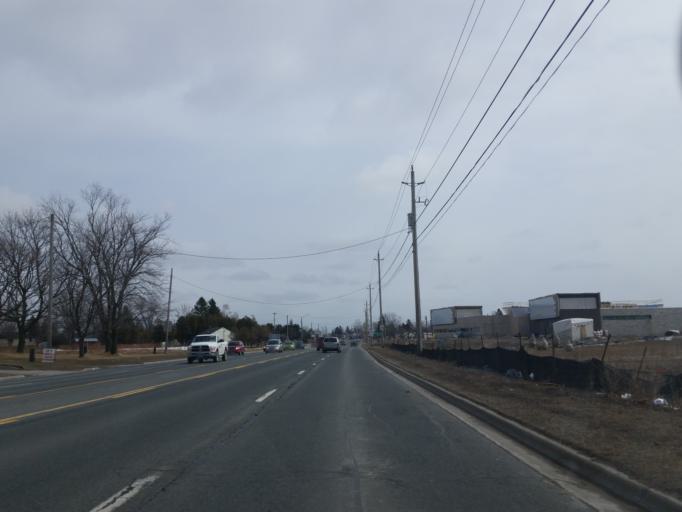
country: CA
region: Ontario
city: Oshawa
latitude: 43.9112
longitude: -78.7272
